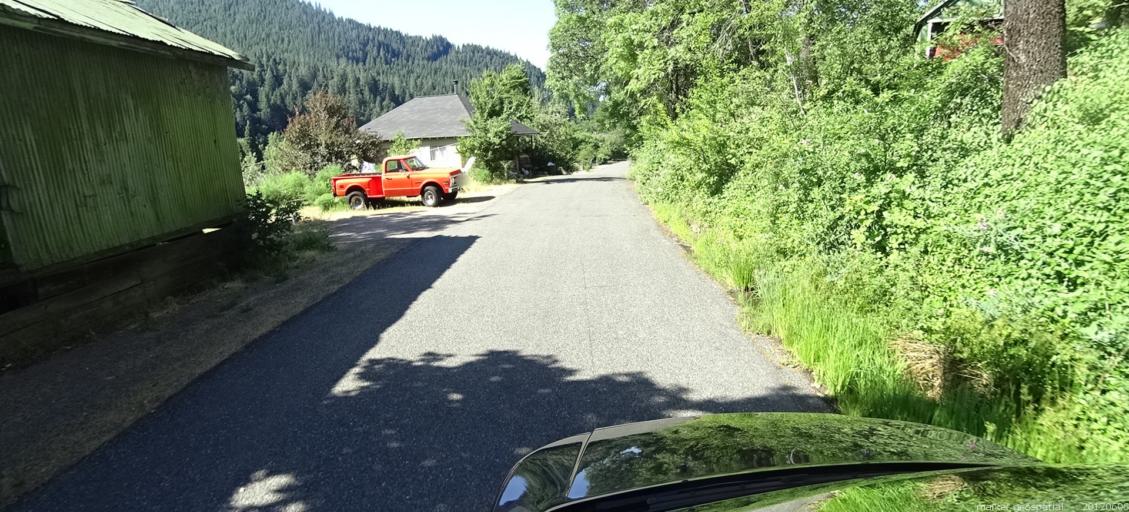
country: US
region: California
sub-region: Siskiyou County
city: Dunsmuir
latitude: 41.2008
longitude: -122.2746
